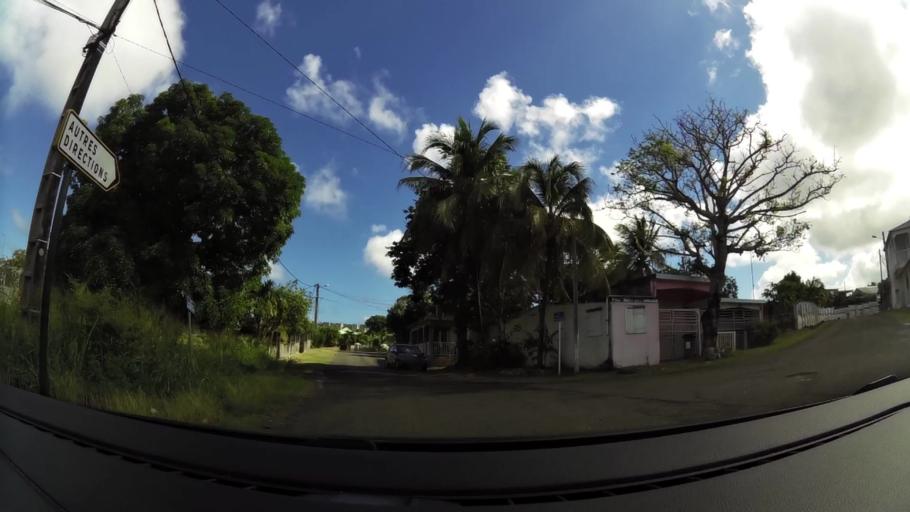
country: GP
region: Guadeloupe
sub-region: Guadeloupe
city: Anse-Bertrand
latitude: 16.4678
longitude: -61.5054
